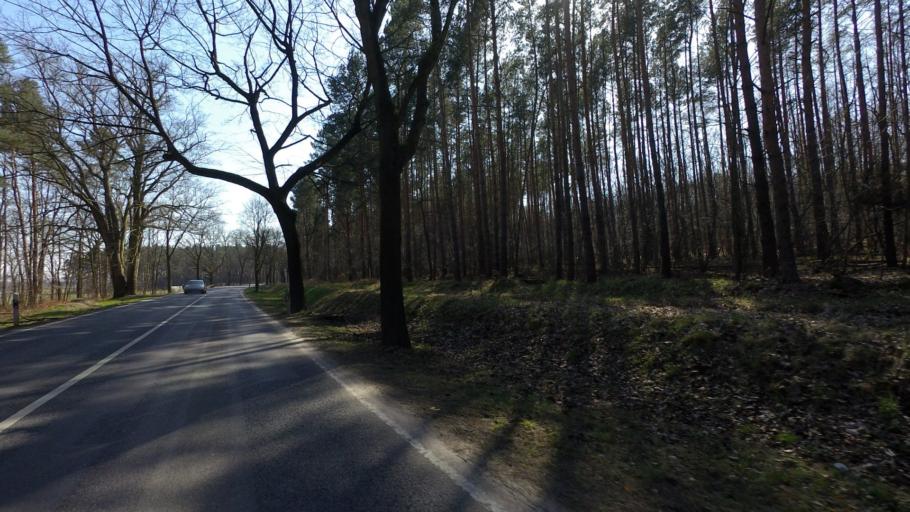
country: DE
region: Brandenburg
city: Leegebruch
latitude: 52.7305
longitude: 13.1804
